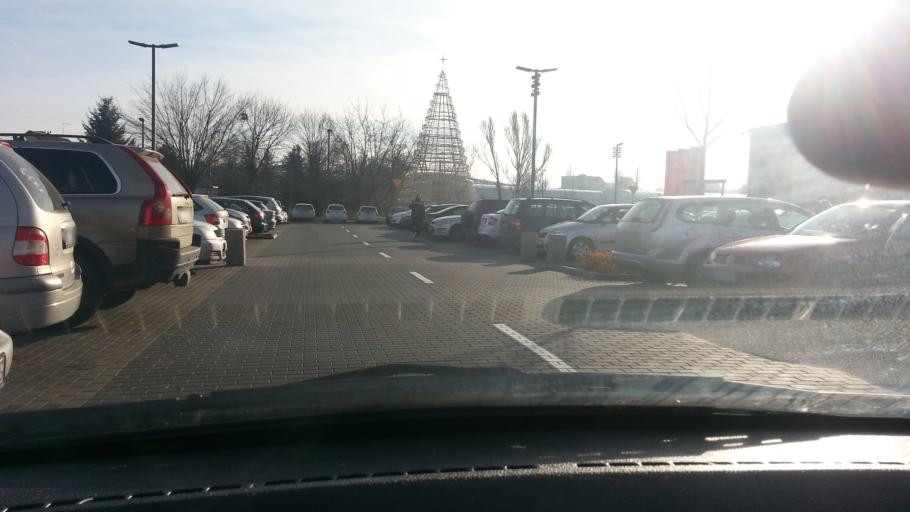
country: PL
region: Masovian Voivodeship
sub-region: Warszawa
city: Targowek
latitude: 52.3004
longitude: 21.0274
